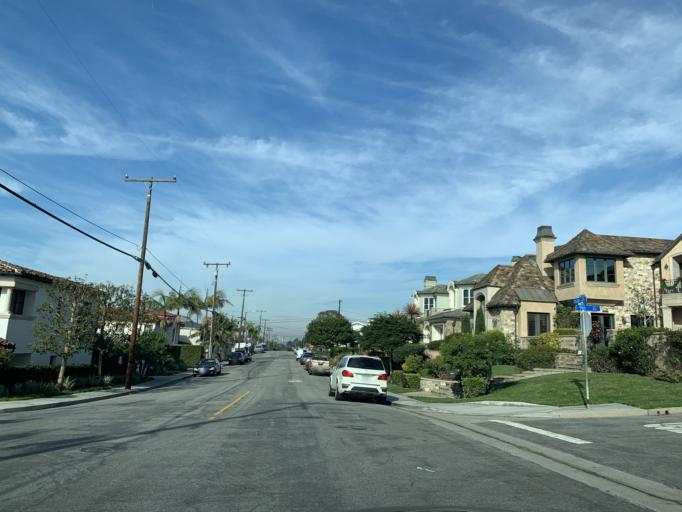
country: US
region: California
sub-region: Los Angeles County
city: Manhattan Beach
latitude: 33.8847
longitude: -118.4033
